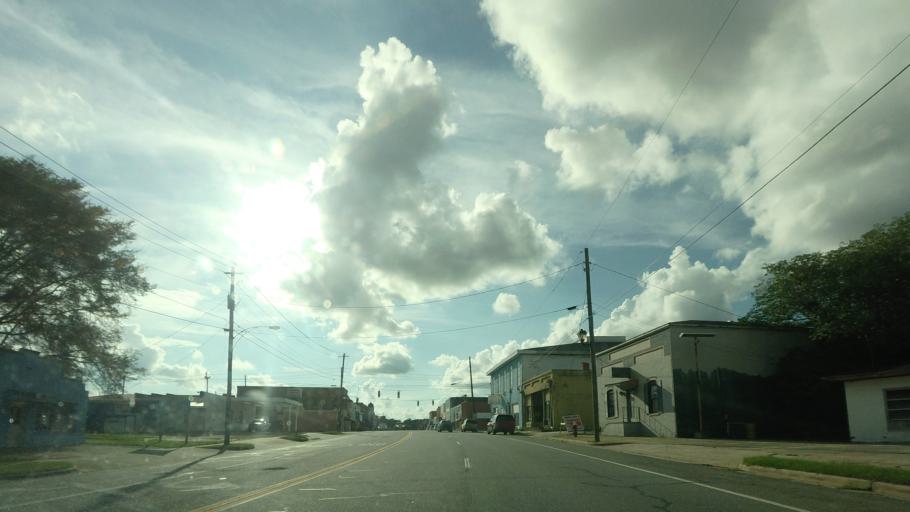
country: US
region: Georgia
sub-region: Pulaski County
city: Hawkinsville
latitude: 32.2836
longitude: -83.4647
